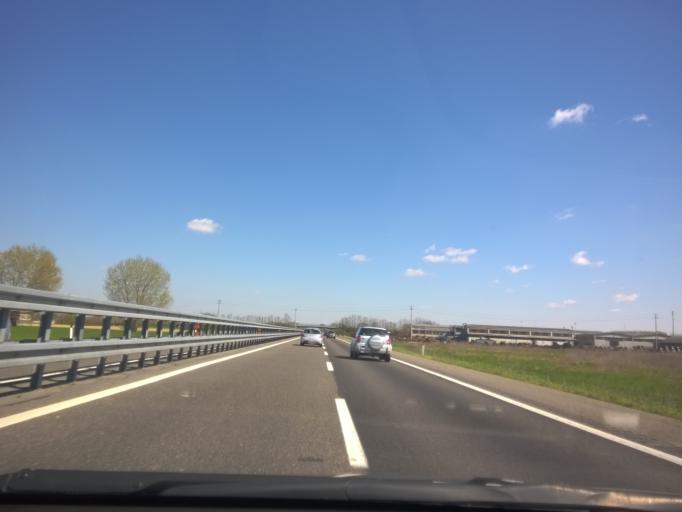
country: IT
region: Lombardy
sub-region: Provincia di Pavia
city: Arena Po
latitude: 45.0844
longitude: 9.3550
